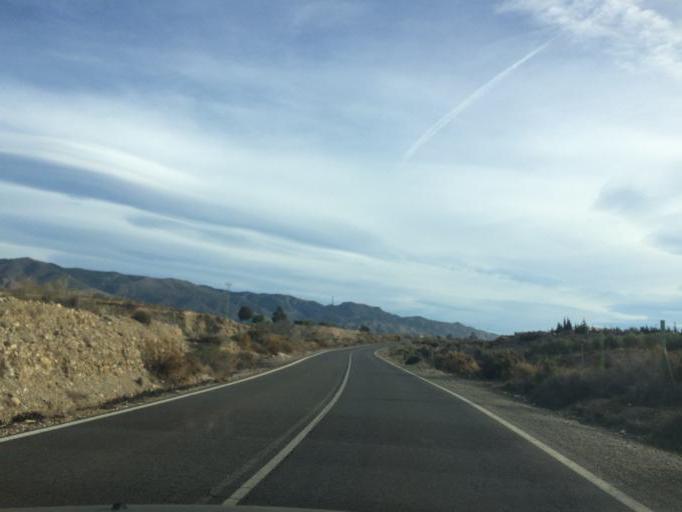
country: ES
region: Andalusia
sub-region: Provincia de Almeria
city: Pechina
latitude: 36.9239
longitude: -2.4422
